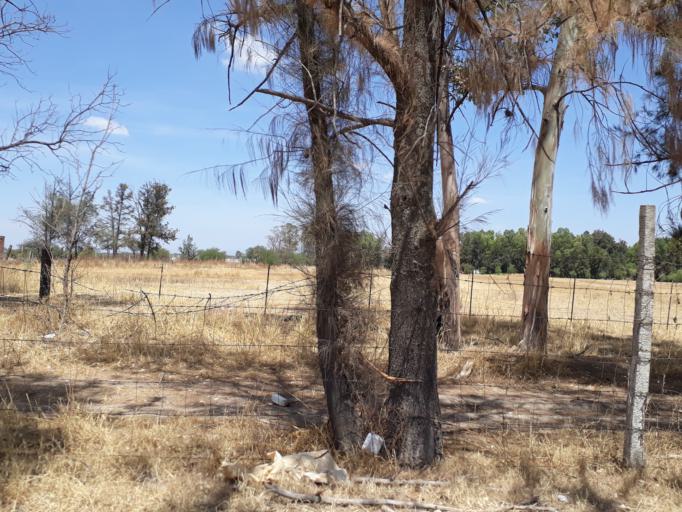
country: MX
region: Aguascalientes
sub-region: Aguascalientes
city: San Sebastian [Fraccionamiento]
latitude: 21.8140
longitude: -102.2931
